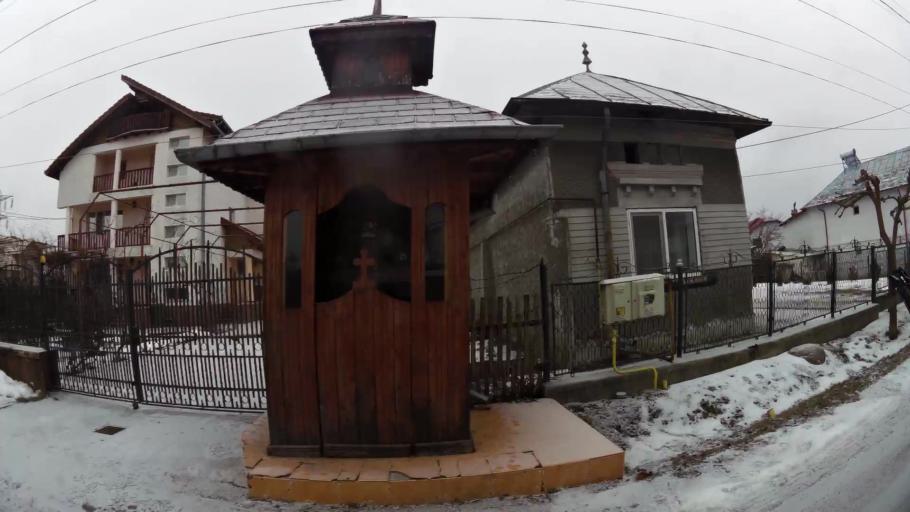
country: RO
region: Dambovita
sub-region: Municipiul Targoviste
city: Targoviste
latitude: 44.9389
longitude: 25.4858
